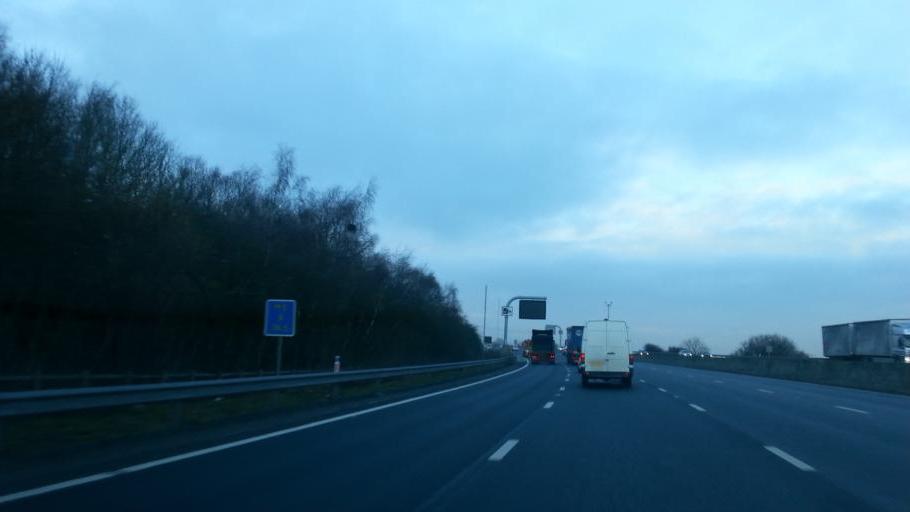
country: GB
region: England
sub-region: Worcestershire
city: Droitwich
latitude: 52.2718
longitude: -2.1246
